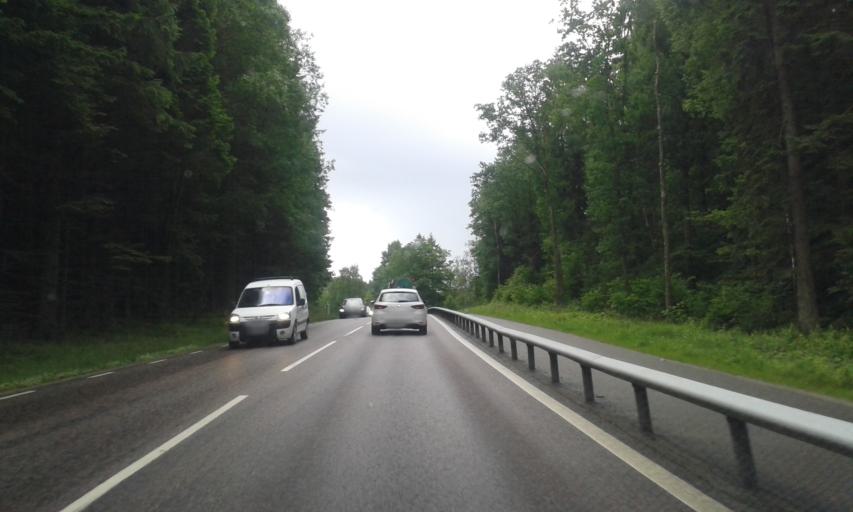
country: SE
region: Vaestra Goetaland
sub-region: Kungalvs Kommun
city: Diserod
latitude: 57.9010
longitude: 12.0074
